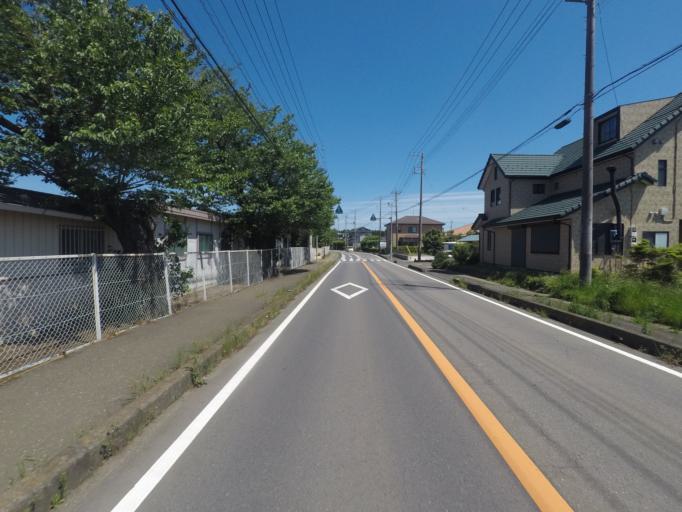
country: JP
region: Ibaraki
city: Ami
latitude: 36.0980
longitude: 140.2437
